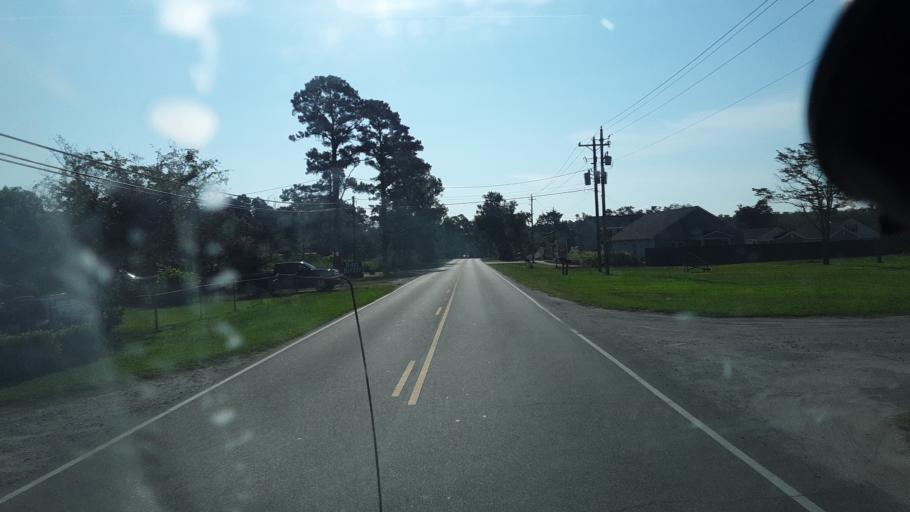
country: US
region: North Carolina
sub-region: Brunswick County
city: Navassa
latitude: 34.2465
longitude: -78.0208
